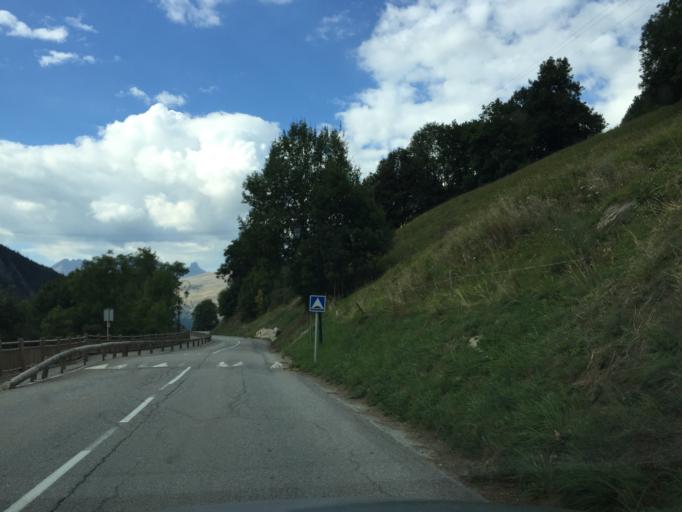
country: FR
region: Rhone-Alpes
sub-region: Departement de la Savoie
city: Belle-Plagne
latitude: 45.5406
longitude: 6.7593
